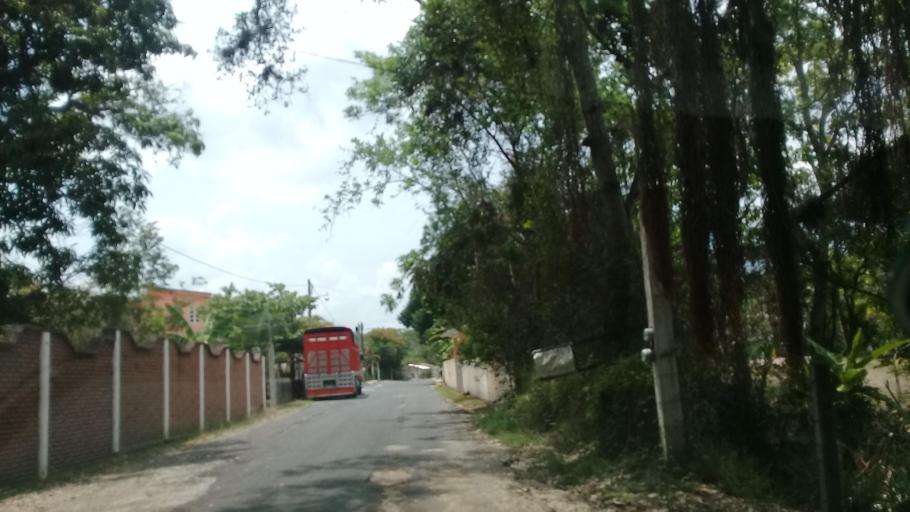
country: MX
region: Veracruz
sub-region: Emiliano Zapata
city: Plan del Rio
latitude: 19.4296
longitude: -96.6977
